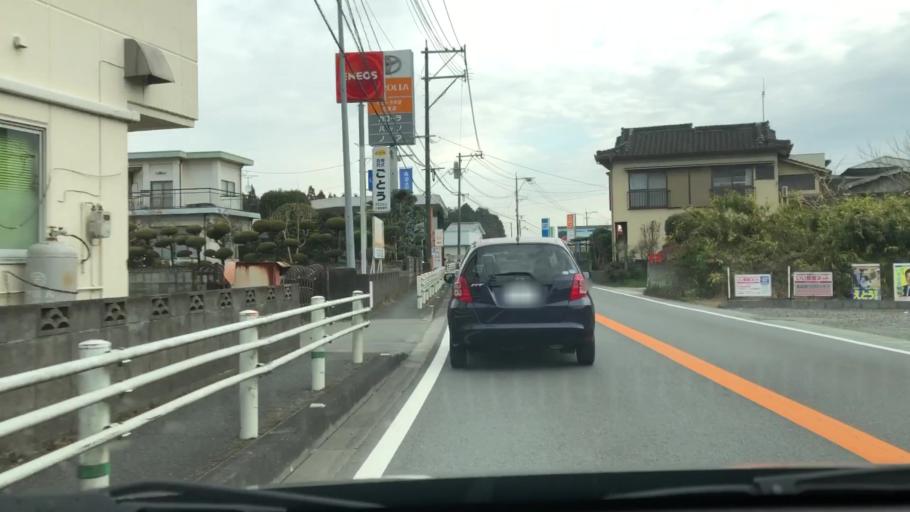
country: JP
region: Oita
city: Takedamachi
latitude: 32.9887
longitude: 131.6054
